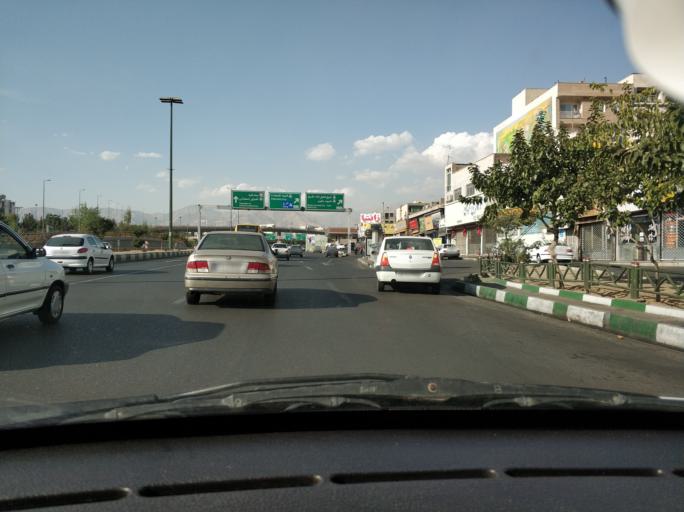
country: IR
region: Tehran
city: Tehran
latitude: 35.7085
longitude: 51.3371
